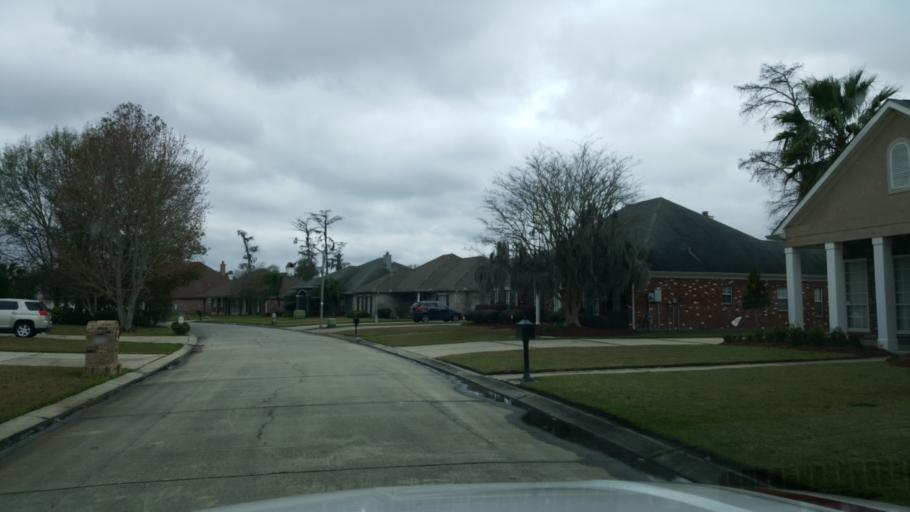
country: US
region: Louisiana
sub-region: Jefferson Parish
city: Woodmere
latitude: 29.8746
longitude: -90.0784
